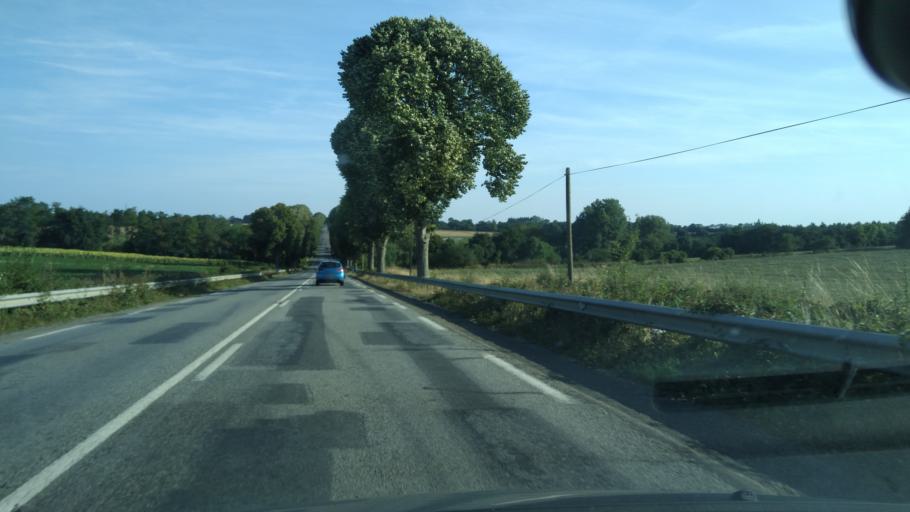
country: FR
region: Pays de la Loire
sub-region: Departement de la Mayenne
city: Chateau-Gontier
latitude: 47.9025
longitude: -0.6843
